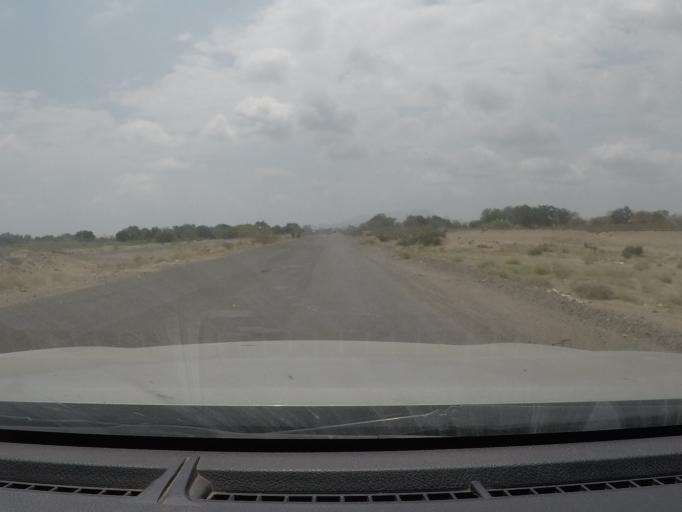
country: YE
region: Aden
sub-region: Ash Shaikh Outhman
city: Ash Shaykh `Uthman
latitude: 12.9176
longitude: 45.0087
